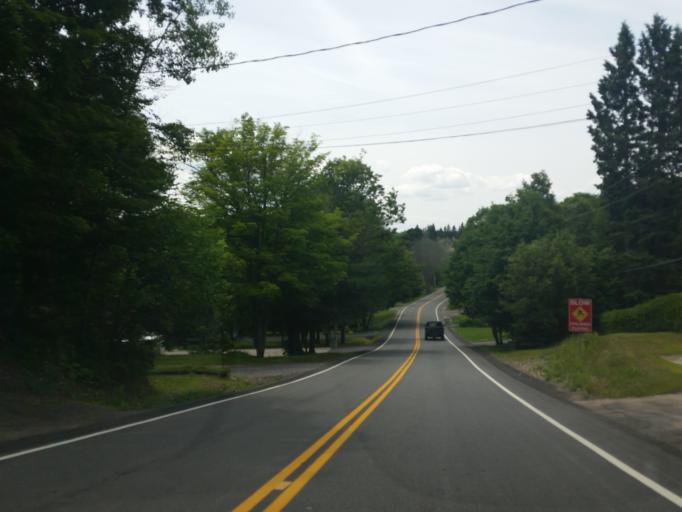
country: CA
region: Ontario
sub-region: Parry Sound District
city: Parry Sound
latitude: 45.3947
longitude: -80.0274
